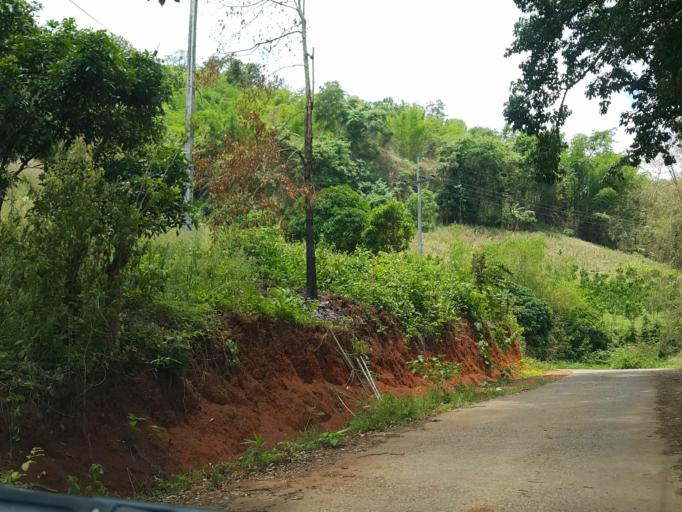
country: TH
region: Chiang Mai
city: Samoeng
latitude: 18.7781
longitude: 98.8349
